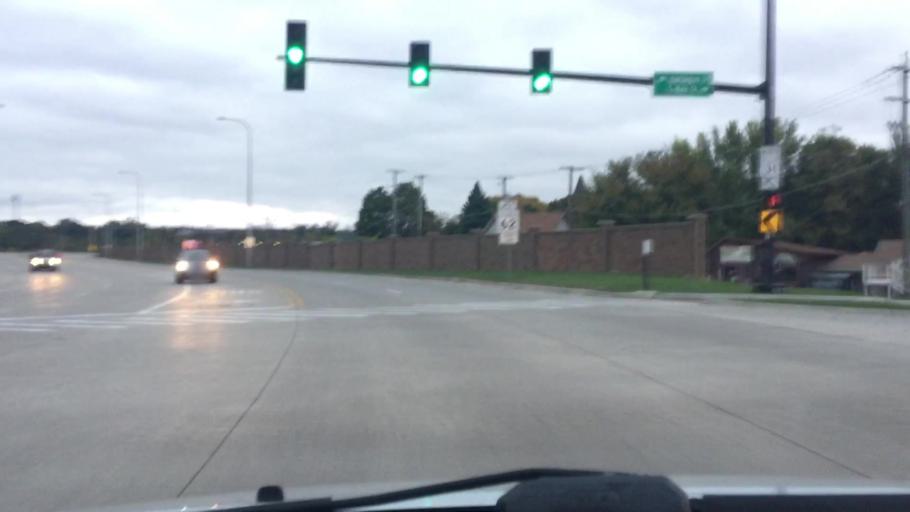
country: US
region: Illinois
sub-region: McHenry County
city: Algonquin
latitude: 42.1642
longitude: -88.2956
